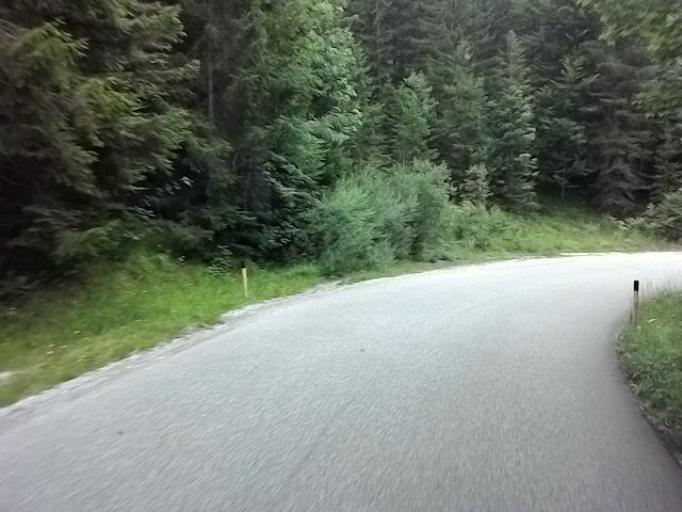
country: DE
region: Bavaria
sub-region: Upper Bavaria
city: Wallgau
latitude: 47.5311
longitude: 11.3046
